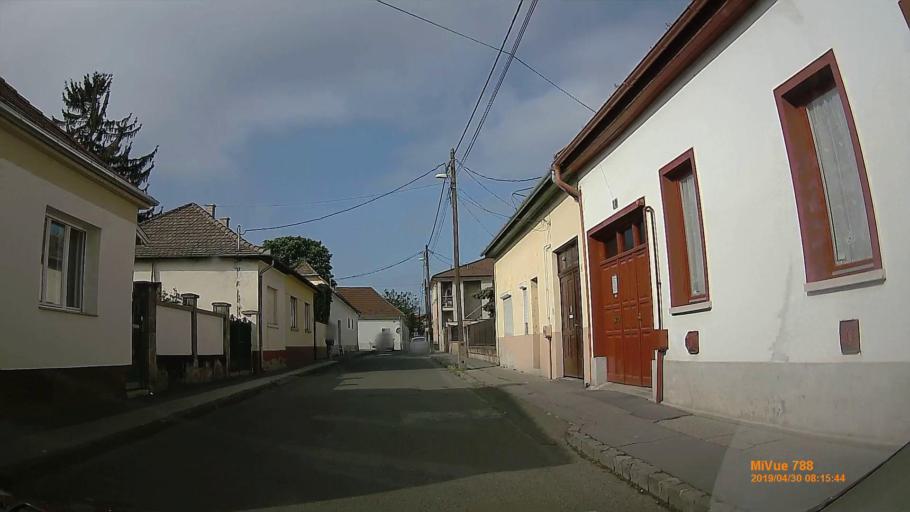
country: HU
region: Pest
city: Vac
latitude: 47.7746
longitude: 19.1343
